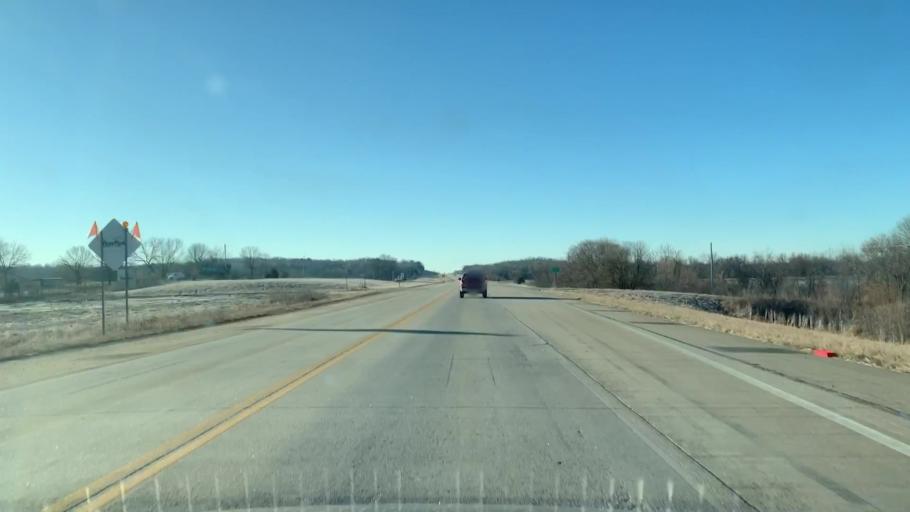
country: US
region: Kansas
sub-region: Crawford County
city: Arma
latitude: 37.6743
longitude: -94.7036
